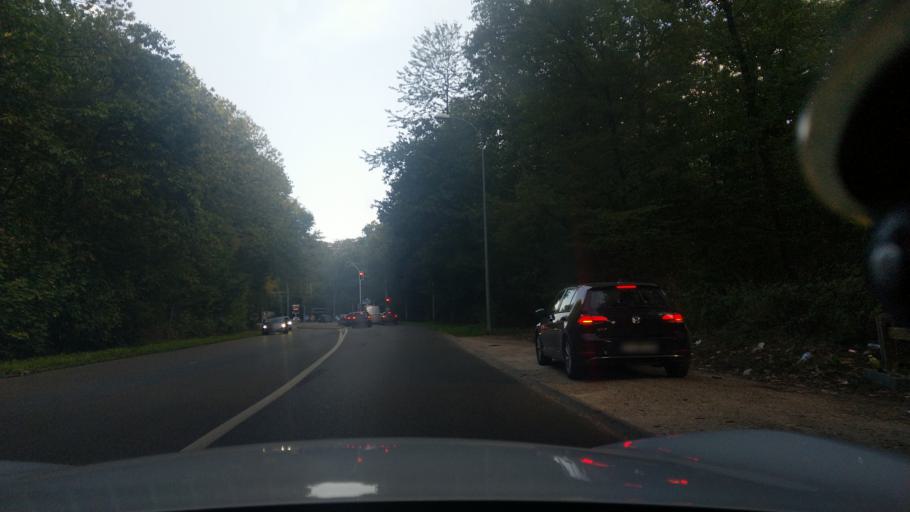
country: FR
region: Ile-de-France
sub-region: Departement des Yvelines
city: La Celle-Saint-Cloud
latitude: 48.8347
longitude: 2.1416
